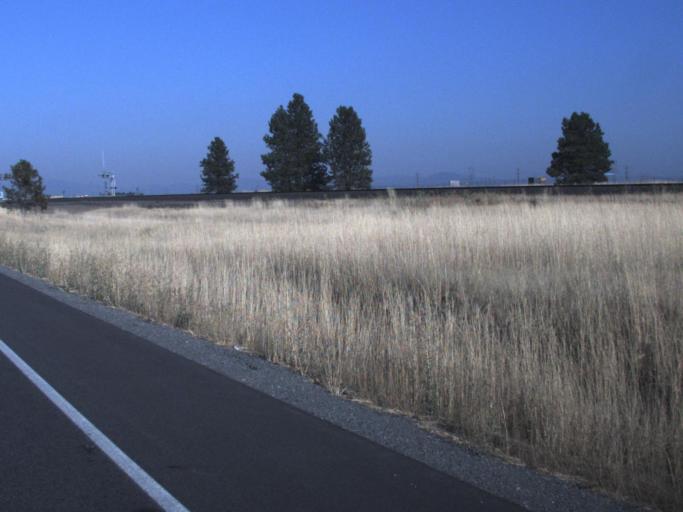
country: US
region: Washington
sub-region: Spokane County
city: Otis Orchards-East Farms
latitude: 47.7320
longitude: -117.0508
